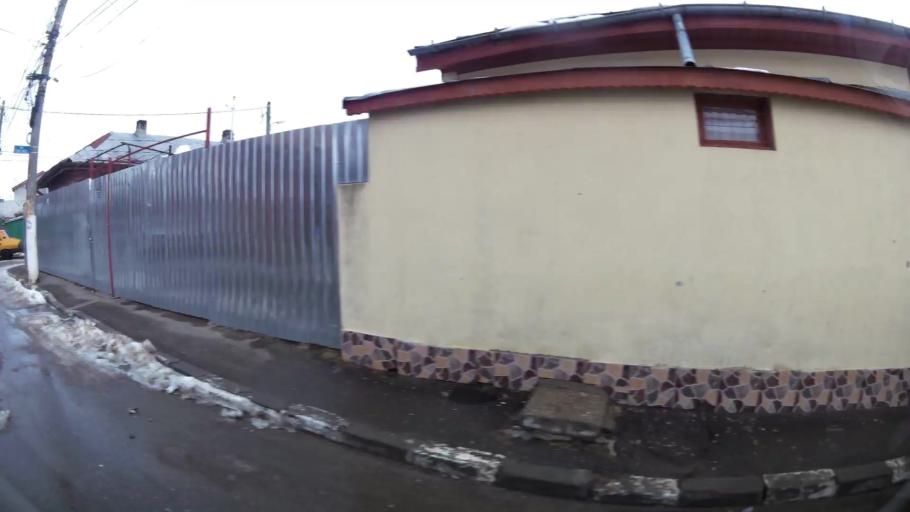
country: RO
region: Ilfov
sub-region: Comuna Pantelimon
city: Pantelimon
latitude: 44.4492
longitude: 26.2116
